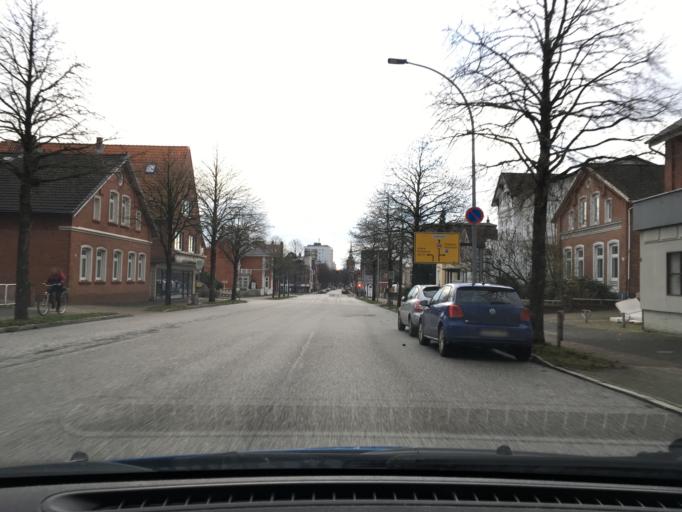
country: DE
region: Schleswig-Holstein
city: Itzehoe
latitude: 53.9303
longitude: 9.5083
